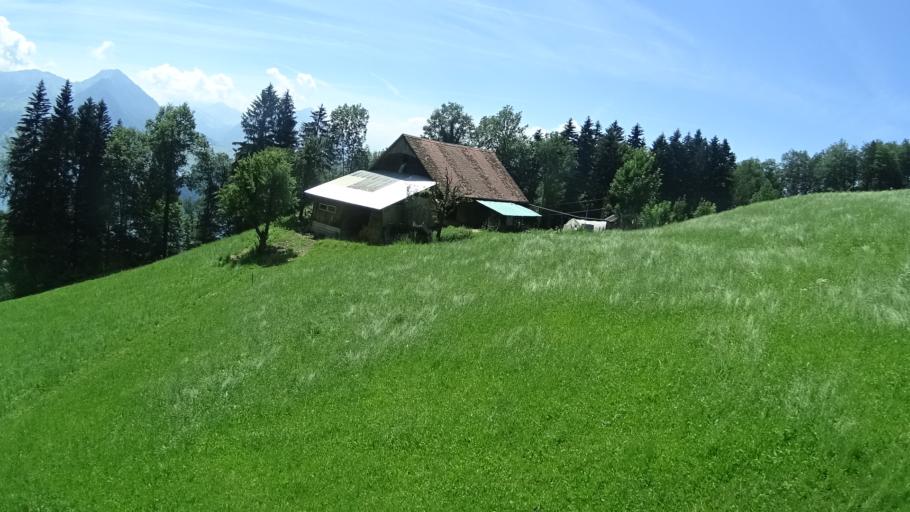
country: CH
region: Lucerne
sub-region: Lucerne-Land District
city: Vitznau
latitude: 47.0242
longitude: 8.4844
